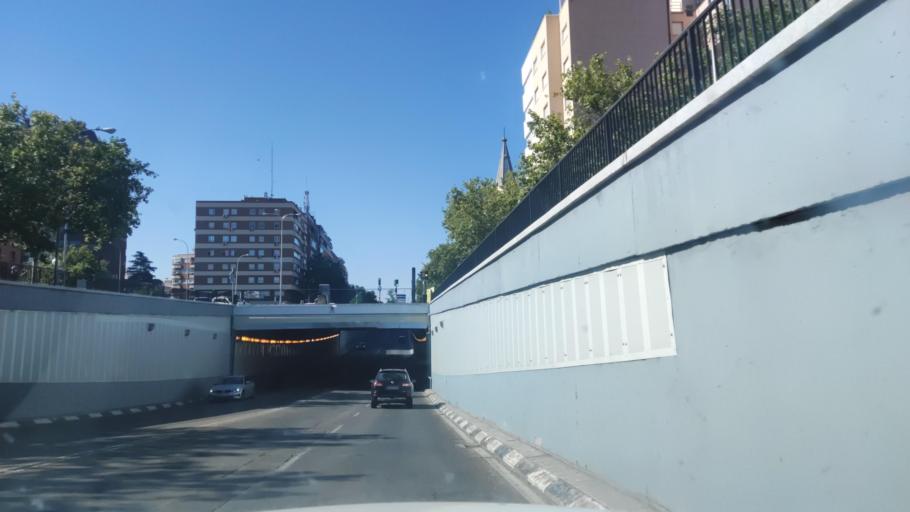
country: ES
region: Madrid
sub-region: Provincia de Madrid
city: Salamanca
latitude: 40.4221
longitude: -3.6689
